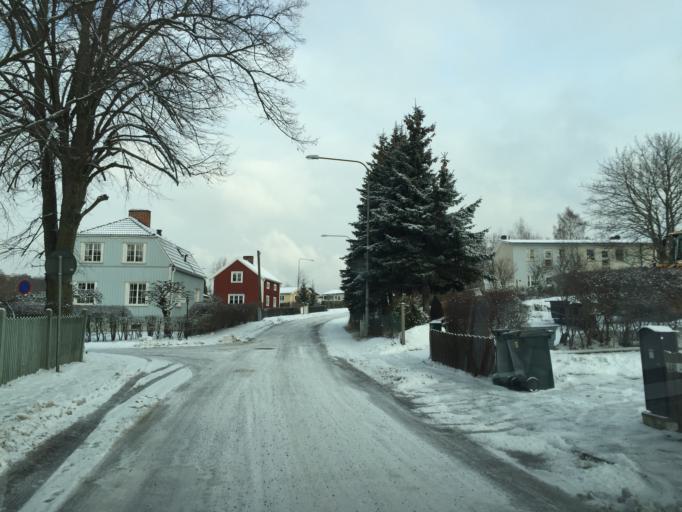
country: SE
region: Stockholm
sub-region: Sodertalje Kommun
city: Soedertaelje
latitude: 59.1971
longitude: 17.6428
